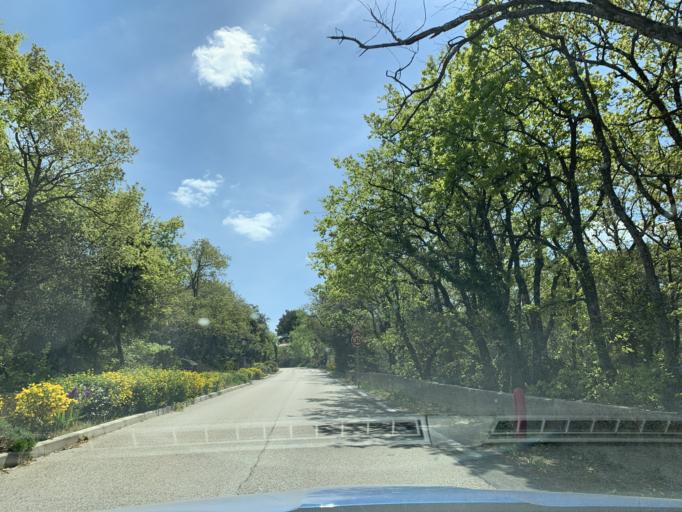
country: FR
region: Provence-Alpes-Cote d'Azur
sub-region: Departement du Vaucluse
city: Saint-Didier
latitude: 43.9773
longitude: 5.1124
